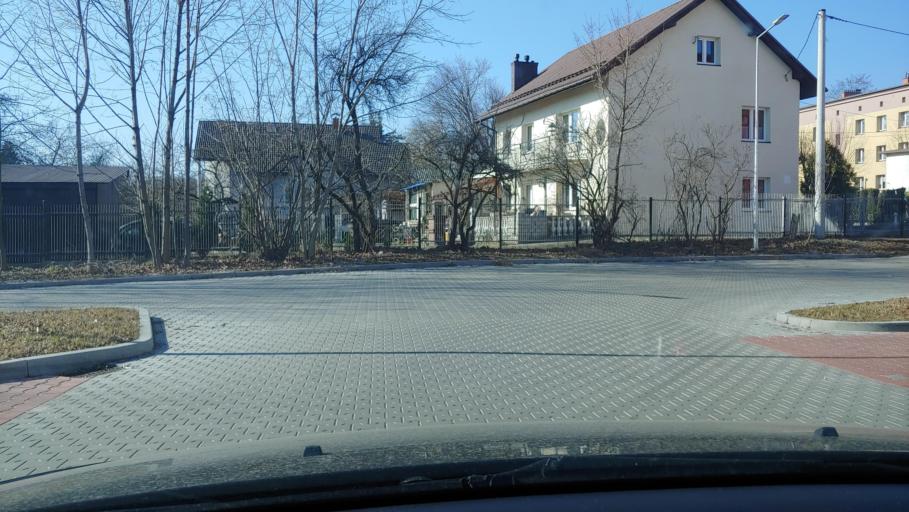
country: PL
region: Lesser Poland Voivodeship
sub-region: Powiat chrzanowski
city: Trzebinia
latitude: 50.1595
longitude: 19.4652
